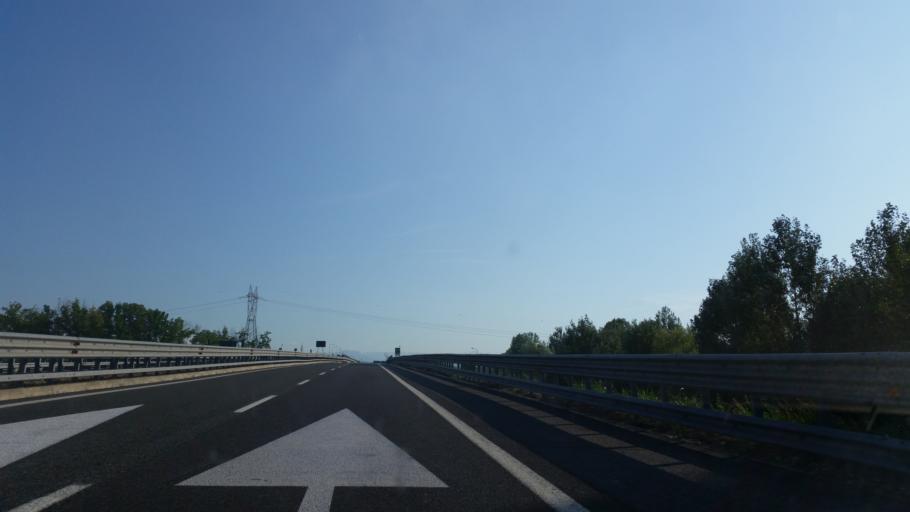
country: IT
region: Piedmont
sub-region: Provincia di Cuneo
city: Sant'Antonio
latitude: 44.7458
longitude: 8.0750
